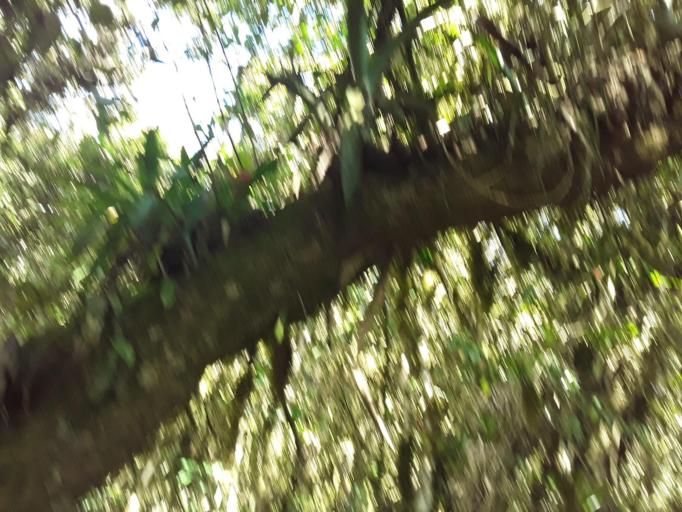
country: BR
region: Minas Gerais
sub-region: Lima Duarte
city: Lima Duarte
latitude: -21.6765
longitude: -43.8824
